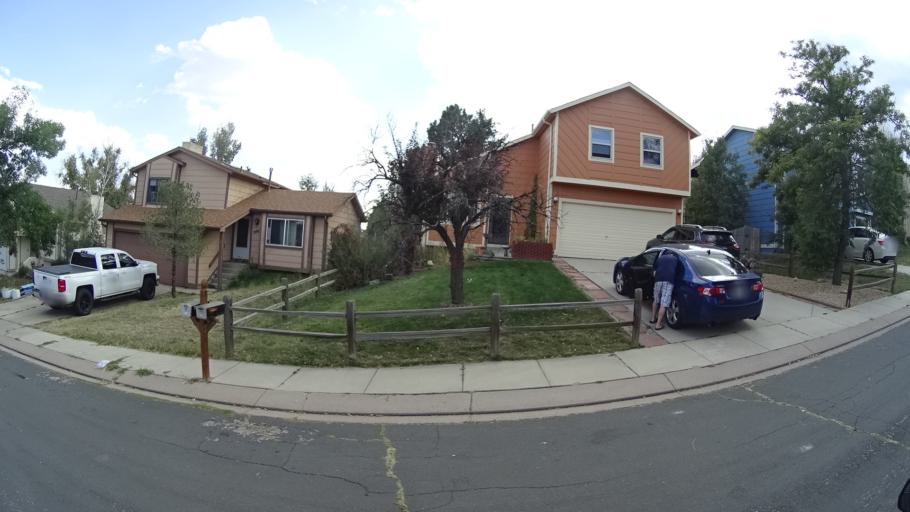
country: US
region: Colorado
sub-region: El Paso County
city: Cimarron Hills
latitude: 38.8764
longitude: -104.7264
